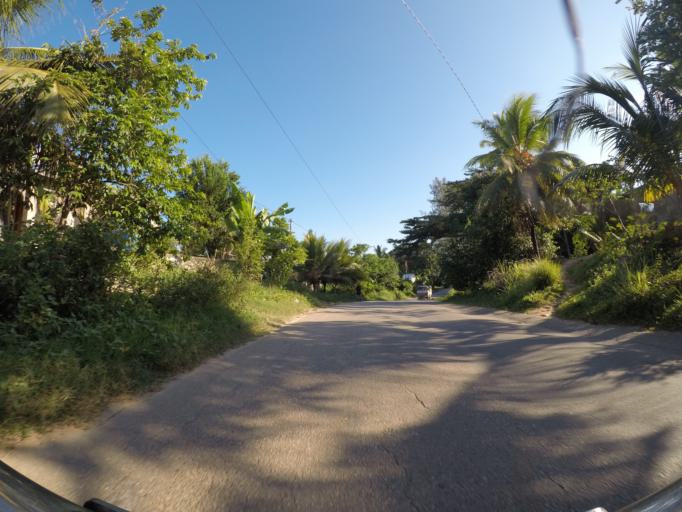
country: TZ
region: Pemba South
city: Chake Chake
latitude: -5.2744
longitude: 39.7707
